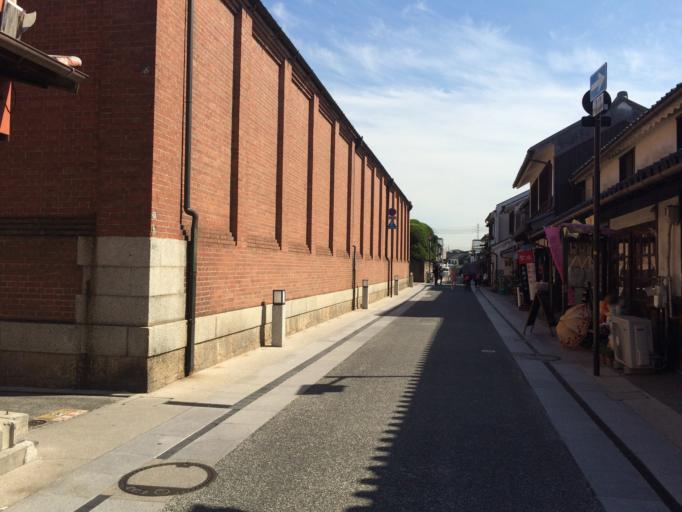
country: JP
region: Okayama
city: Kurashiki
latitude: 34.5958
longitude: 133.7726
